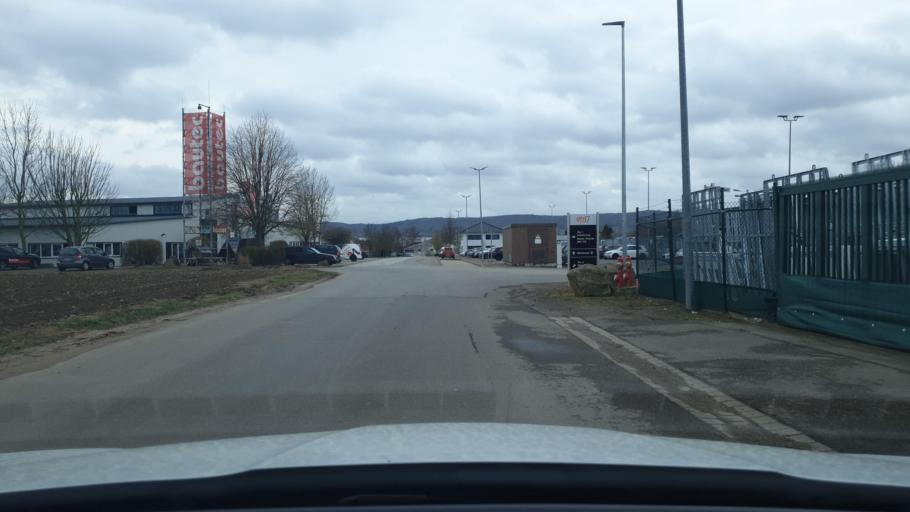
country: DE
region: North Rhine-Westphalia
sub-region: Regierungsbezirk Detmold
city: Hille
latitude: 52.3275
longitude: 8.7492
